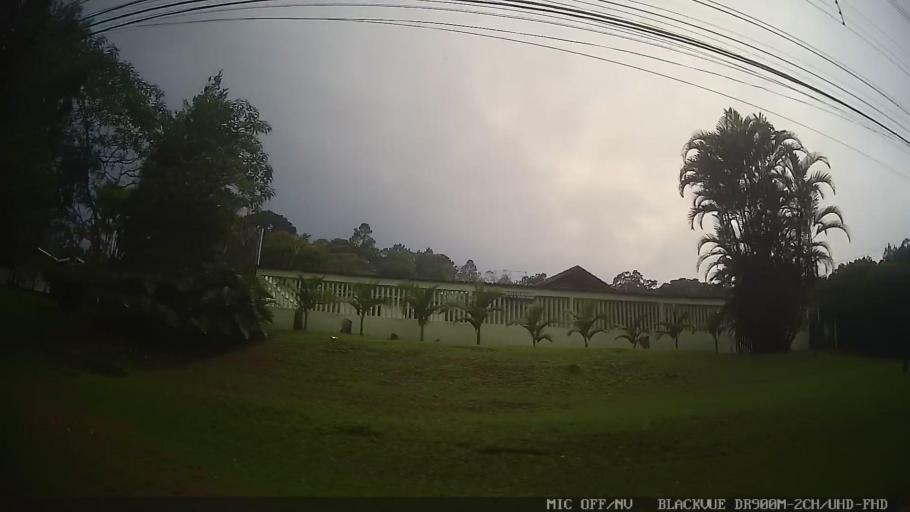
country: BR
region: Sao Paulo
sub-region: Rio Grande Da Serra
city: Rio Grande da Serra
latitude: -23.6879
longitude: -46.3046
